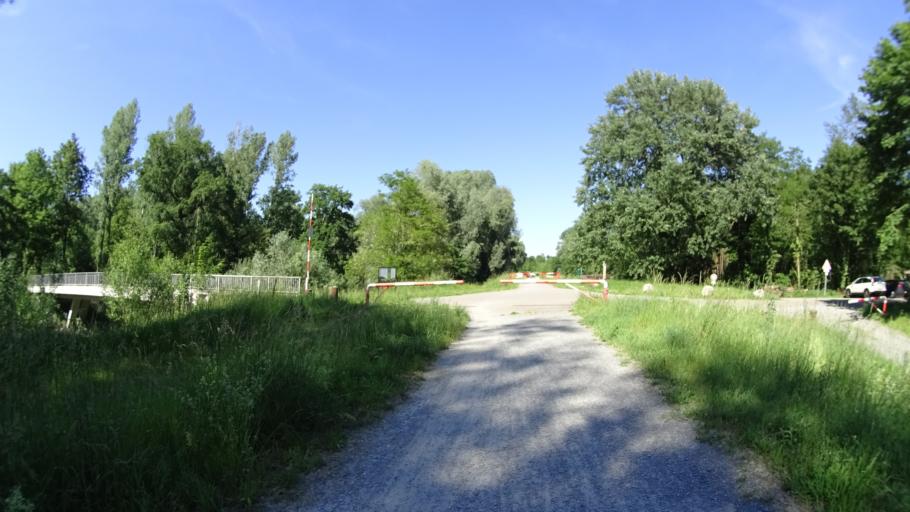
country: DE
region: Baden-Wuerttemberg
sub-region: Karlsruhe Region
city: Eggenstein-Leopoldshafen
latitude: 49.0862
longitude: 8.3588
